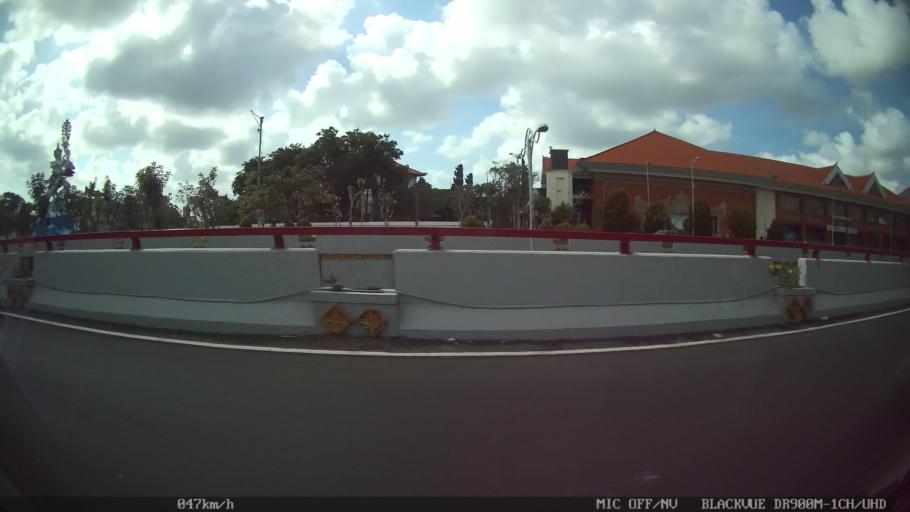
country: ID
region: Bali
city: Jabajero
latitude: -8.7218
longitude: 115.1815
